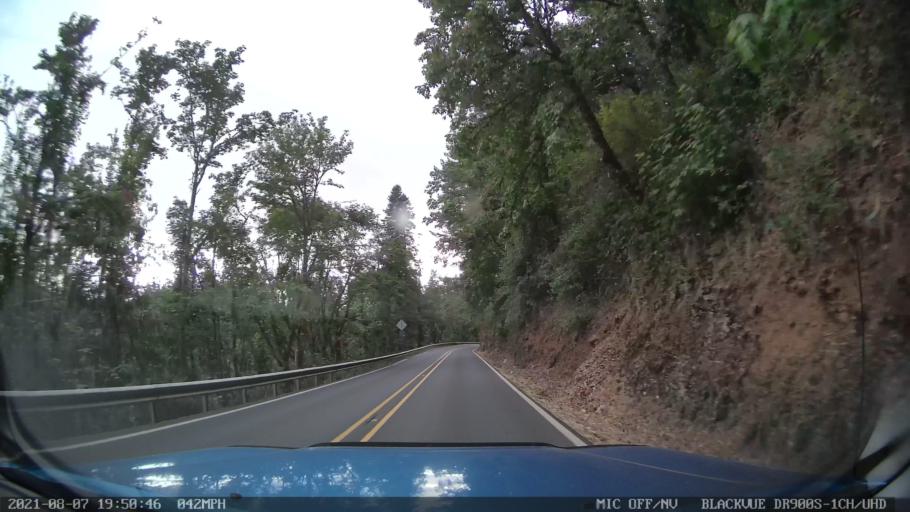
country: US
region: Oregon
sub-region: Marion County
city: Silverton
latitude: 44.9849
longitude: -122.7424
